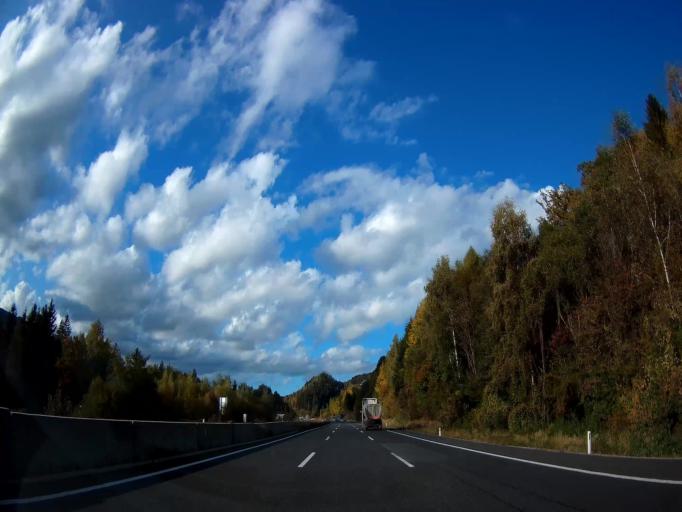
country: AT
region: Carinthia
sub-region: Politischer Bezirk Wolfsberg
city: Wolfsberg
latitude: 46.8811
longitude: 14.8305
